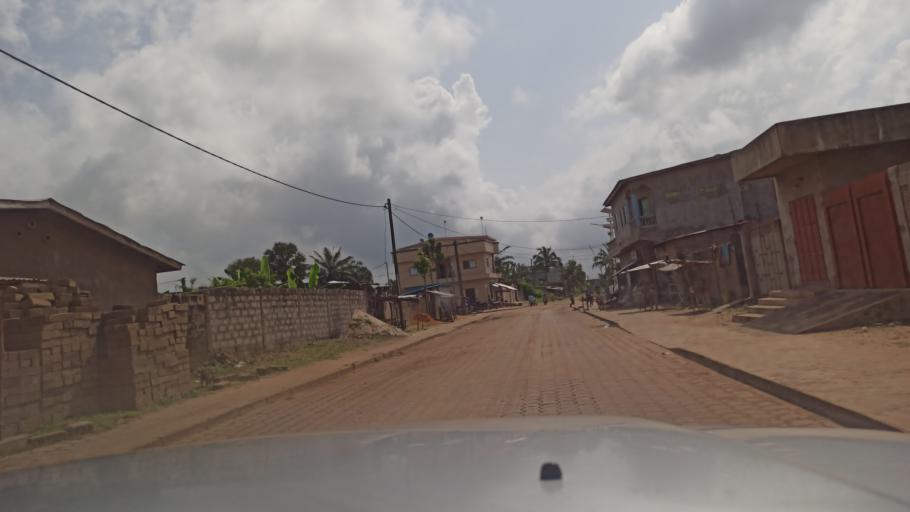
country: BJ
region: Queme
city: Porto-Novo
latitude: 6.4664
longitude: 2.6541
